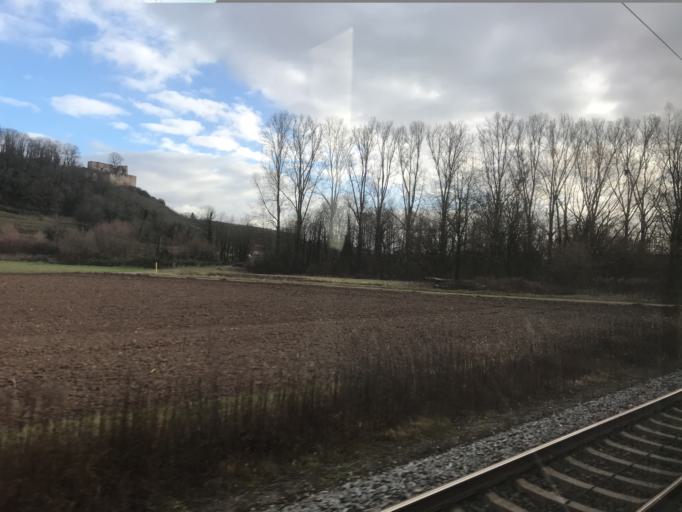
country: DE
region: Baden-Wuerttemberg
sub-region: Freiburg Region
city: Kenzingen
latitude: 48.1749
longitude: 7.7618
